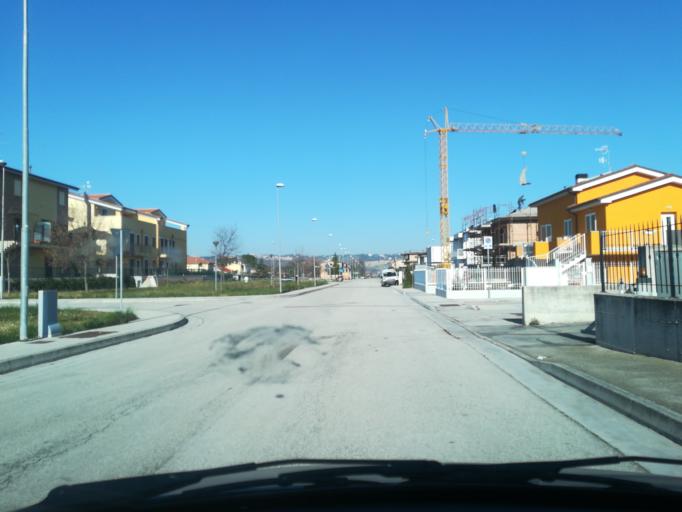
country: IT
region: The Marches
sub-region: Provincia di Macerata
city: Zona Industriale
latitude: 43.2617
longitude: 13.4967
